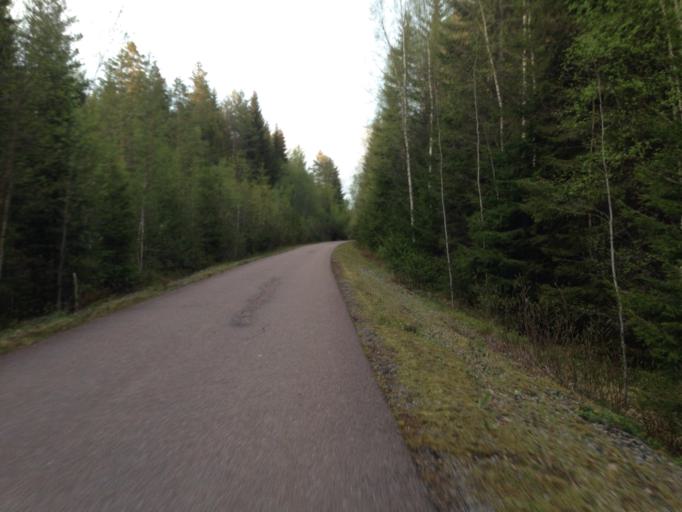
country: SE
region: Dalarna
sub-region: Ludvika Kommun
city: Grangesberg
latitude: 60.1371
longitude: 15.0754
